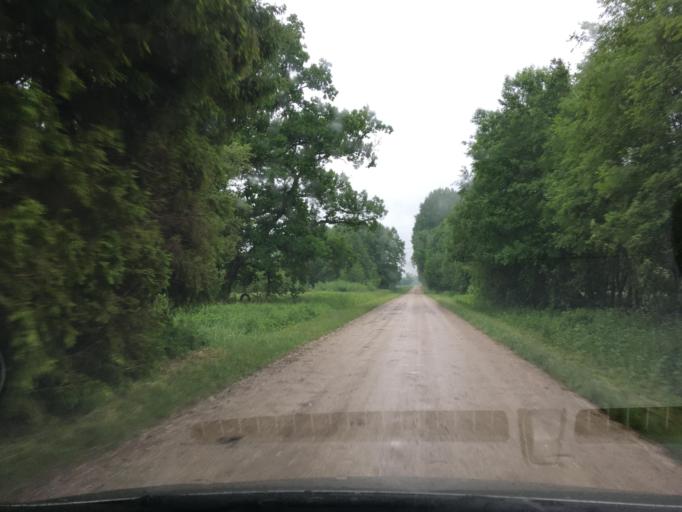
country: EE
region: Laeaene
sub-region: Lihula vald
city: Lihula
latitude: 58.6297
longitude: 23.8145
